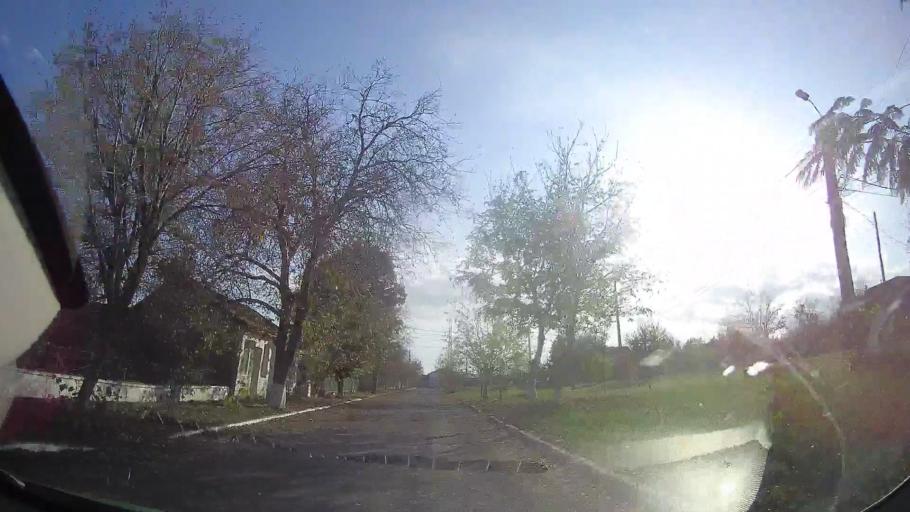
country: RO
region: Constanta
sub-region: Comuna Limanu
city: Limanu
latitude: 43.7958
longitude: 28.5302
